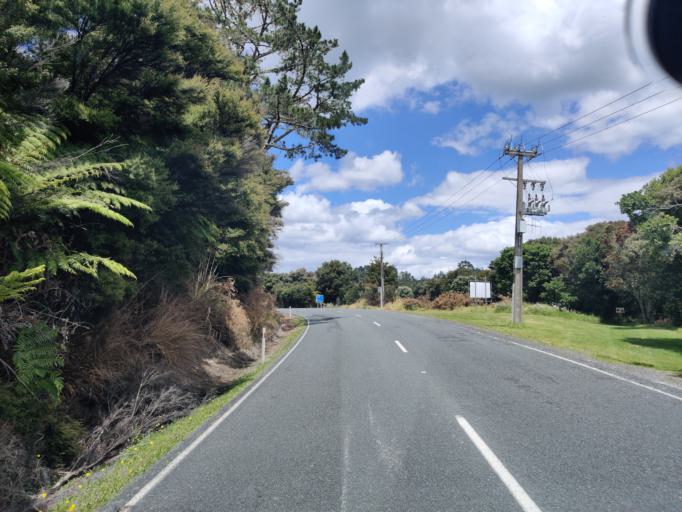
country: NZ
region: Northland
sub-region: Far North District
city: Paihia
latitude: -35.2843
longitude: 174.1474
